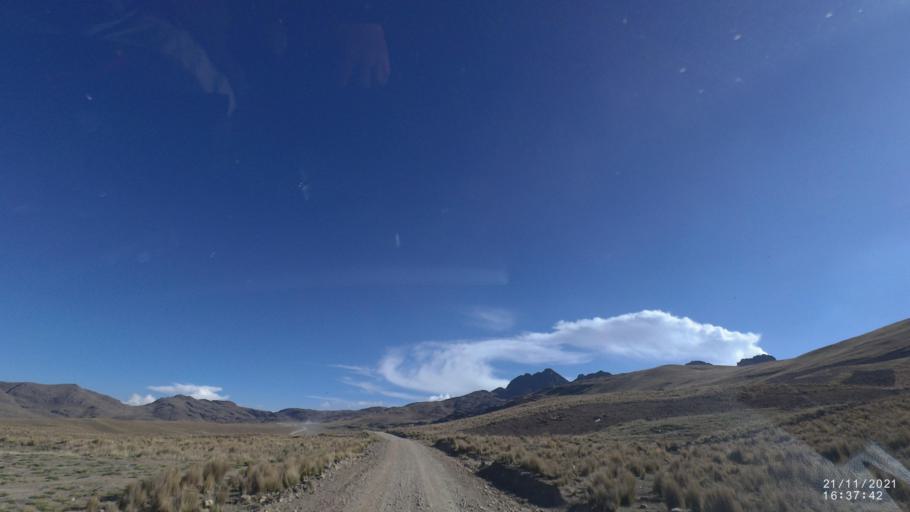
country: BO
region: Cochabamba
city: Cochabamba
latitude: -17.0466
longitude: -66.2635
